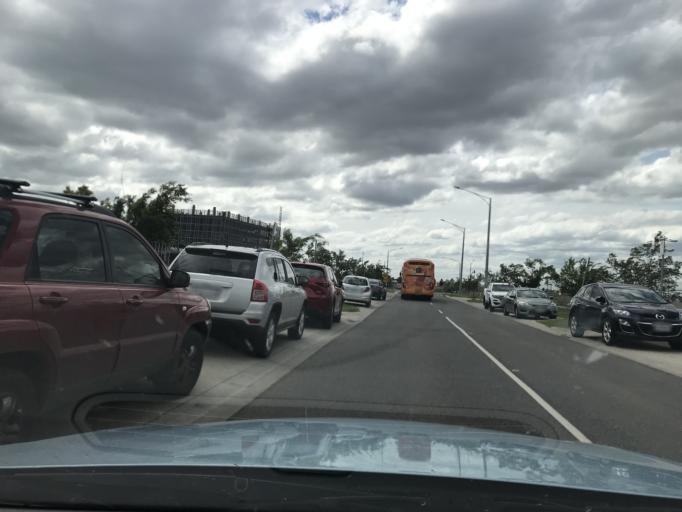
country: AU
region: Victoria
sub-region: Wyndham
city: Williams Landing
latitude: -37.8686
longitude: 144.7459
